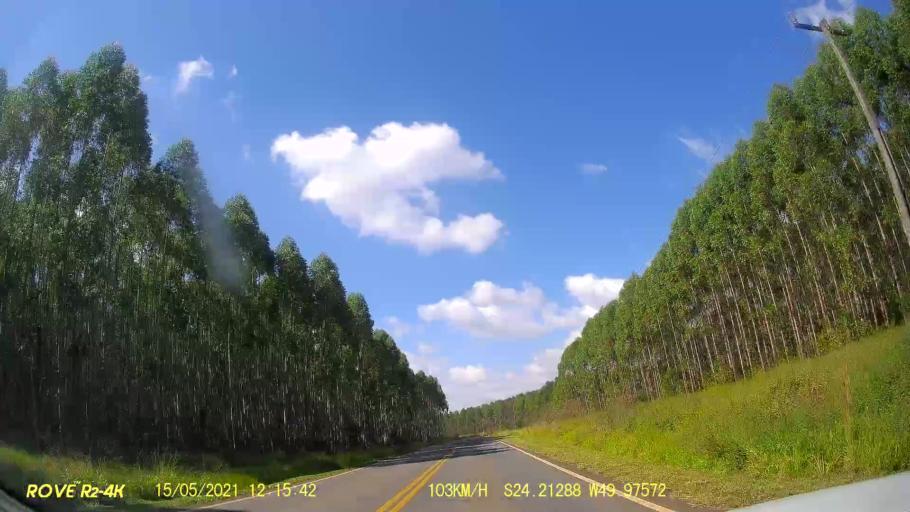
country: BR
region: Parana
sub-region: Jaguariaiva
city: Jaguariaiva
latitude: -24.2129
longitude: -49.9757
